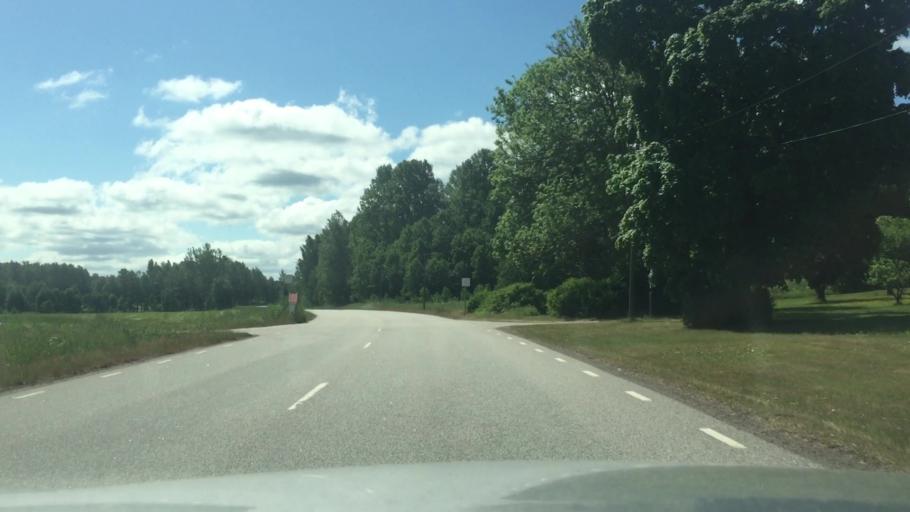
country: SE
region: Vaestra Goetaland
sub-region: Karlsborgs Kommun
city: Molltorp
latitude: 58.6296
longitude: 14.3883
